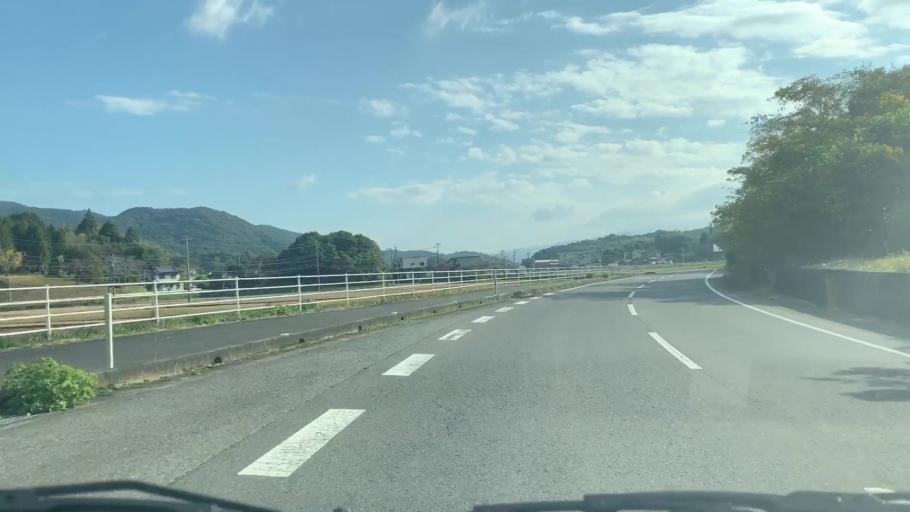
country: JP
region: Saga Prefecture
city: Takeocho-takeo
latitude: 33.1616
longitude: 130.0613
